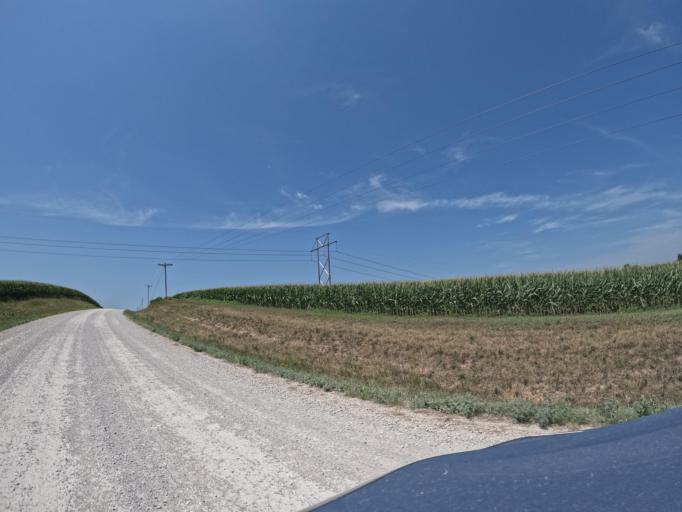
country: US
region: Iowa
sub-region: Henry County
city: Mount Pleasant
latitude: 40.9270
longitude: -91.6381
